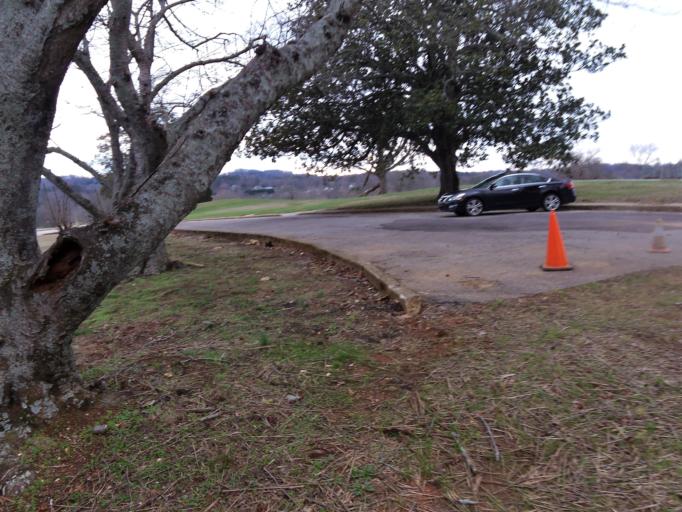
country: US
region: Tennessee
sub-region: Knox County
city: Knoxville
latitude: 35.9221
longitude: -83.9929
